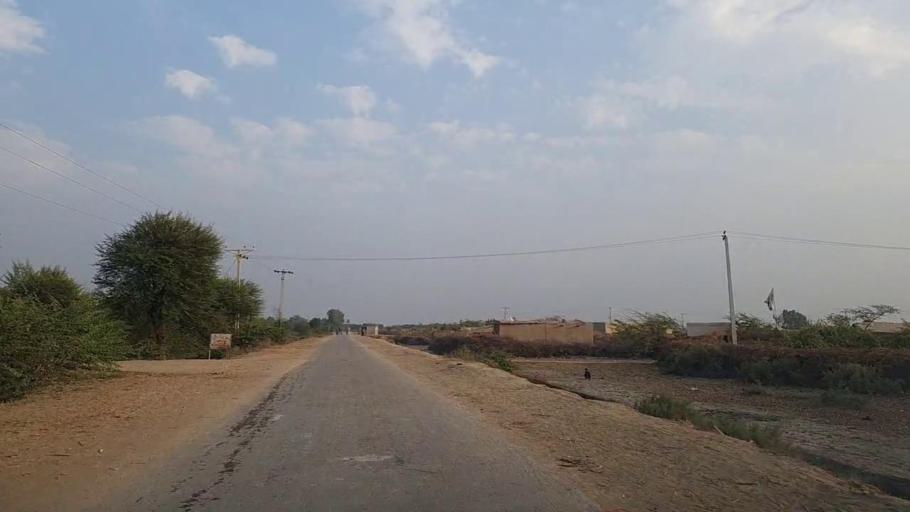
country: PK
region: Sindh
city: Samaro
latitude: 25.2909
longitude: 69.2333
